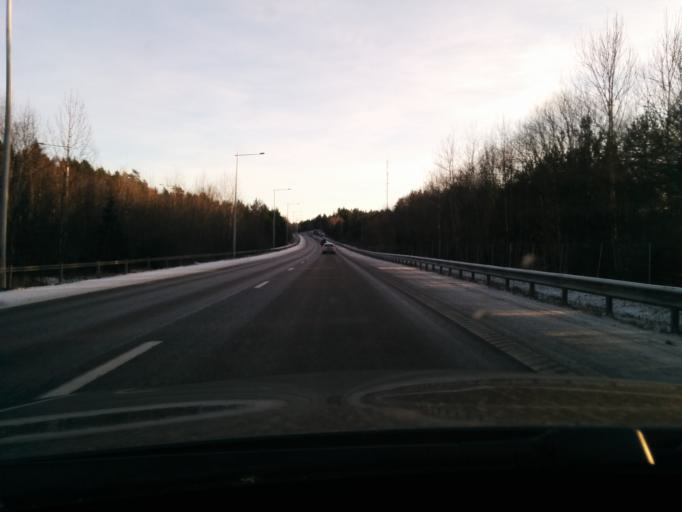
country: SE
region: Stockholm
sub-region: Upplands-Bro Kommun
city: Bro
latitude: 59.5140
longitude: 17.6786
